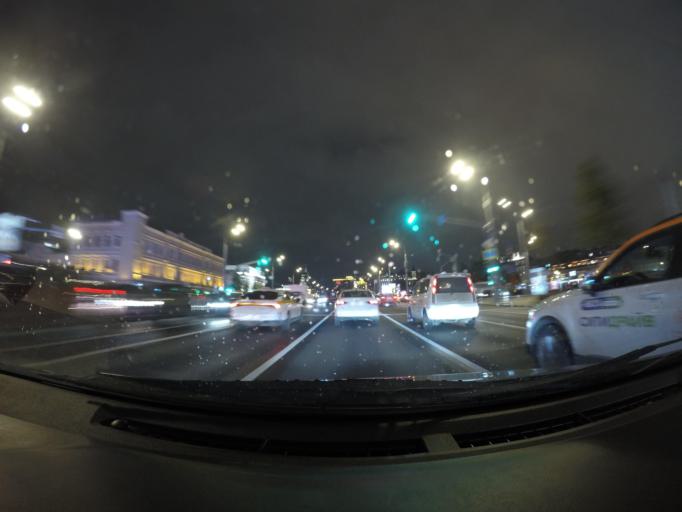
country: RU
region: Moscow
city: Moscow
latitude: 55.7728
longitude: 37.6317
